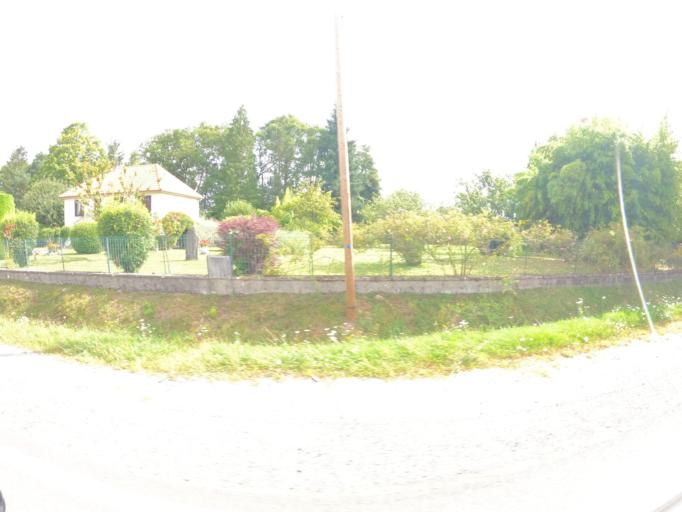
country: FR
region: Limousin
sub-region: Departement de la Haute-Vienne
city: Neuvic-Entier
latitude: 45.7425
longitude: 1.6058
